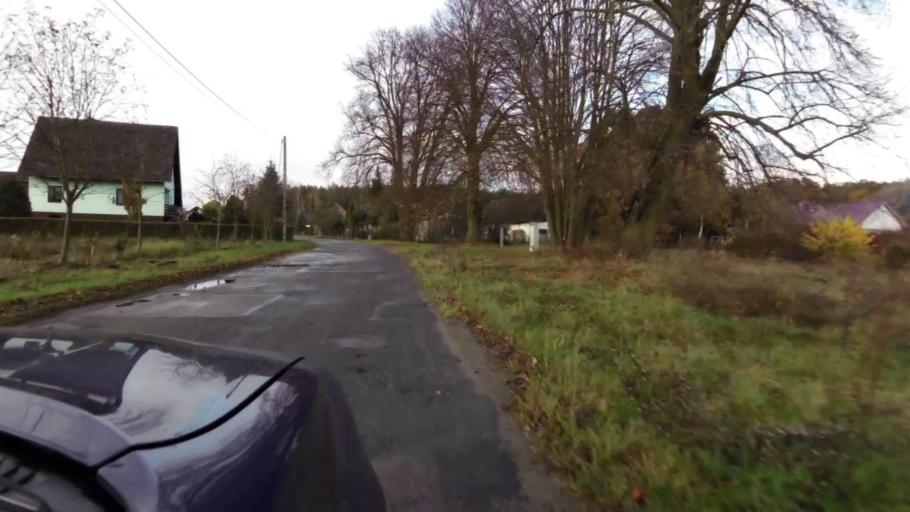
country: PL
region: West Pomeranian Voivodeship
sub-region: Powiat goleniowski
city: Goleniow
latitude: 53.6024
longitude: 14.7548
